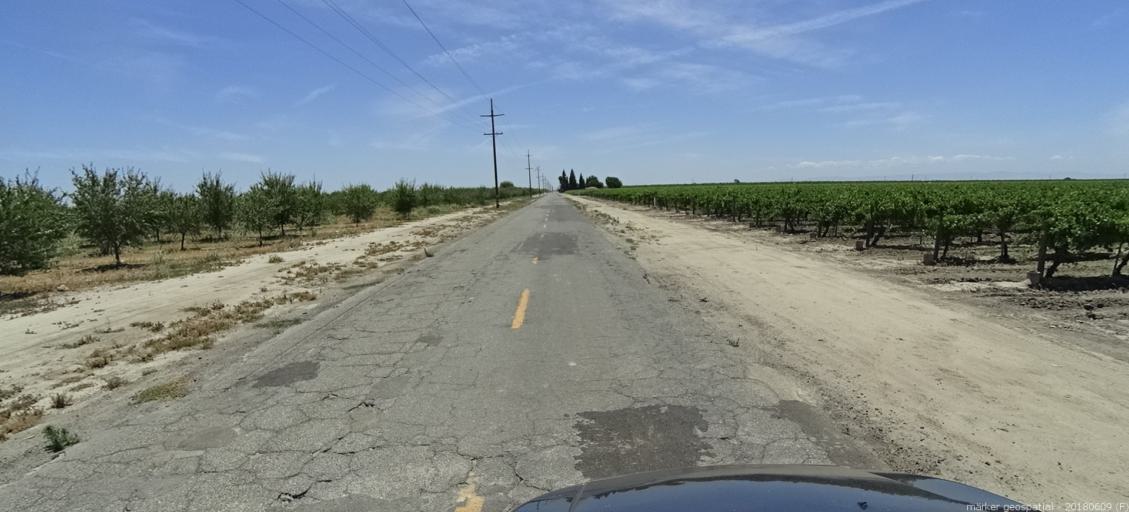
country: US
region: California
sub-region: Madera County
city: Parkwood
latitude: 36.8566
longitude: -120.1103
